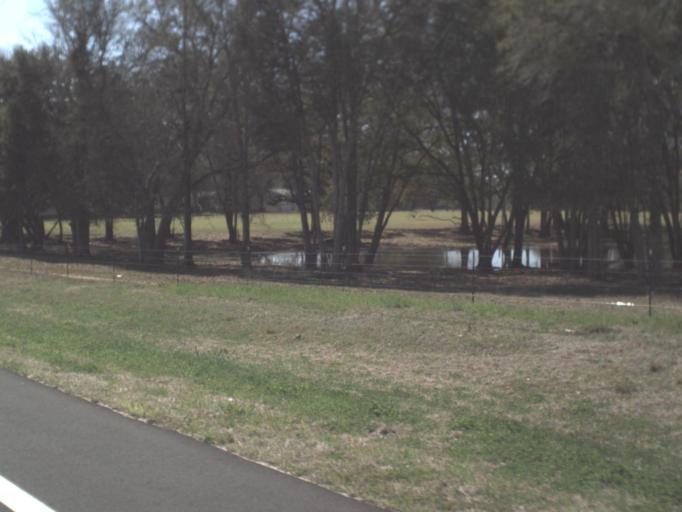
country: US
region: Florida
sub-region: Jackson County
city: Sneads
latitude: 30.7533
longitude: -85.0195
